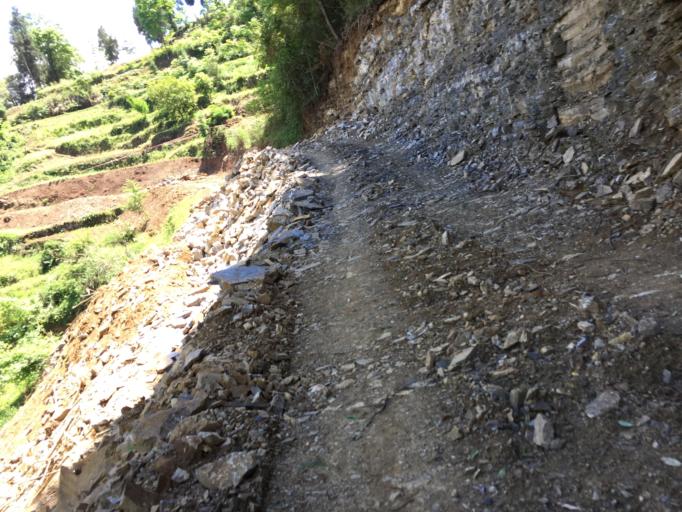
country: CN
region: Guizhou Sheng
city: Shiqian
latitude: 27.6745
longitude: 108.0836
